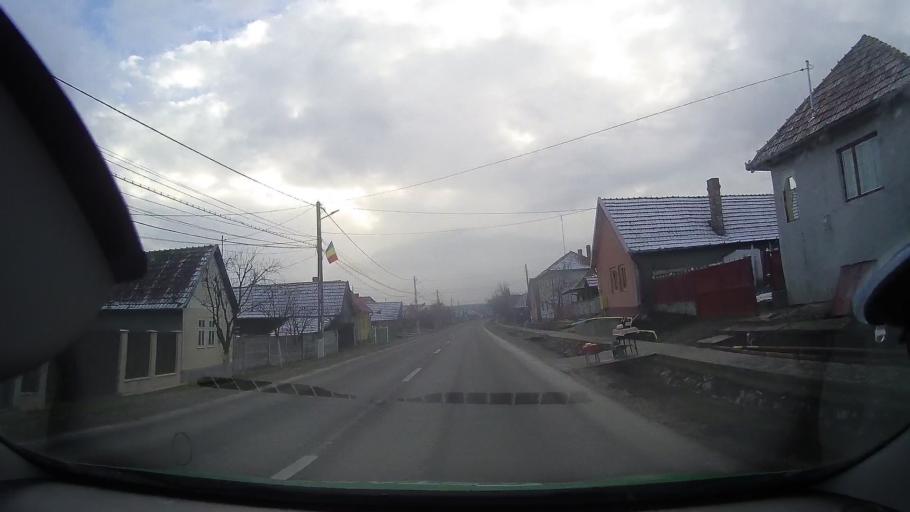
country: RO
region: Mures
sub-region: Comuna Cucerdea
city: Cucerdea
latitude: 46.4005
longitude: 24.2614
